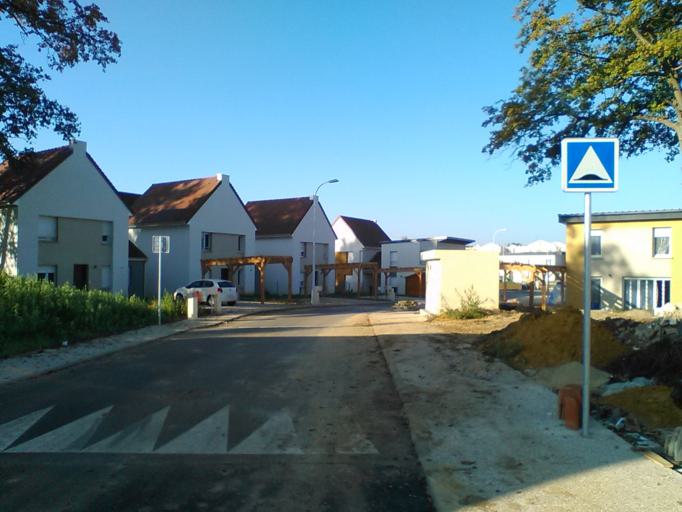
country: FR
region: Ile-de-France
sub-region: Departement de l'Essonne
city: Fleury-Merogis
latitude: 48.6308
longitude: 2.3429
